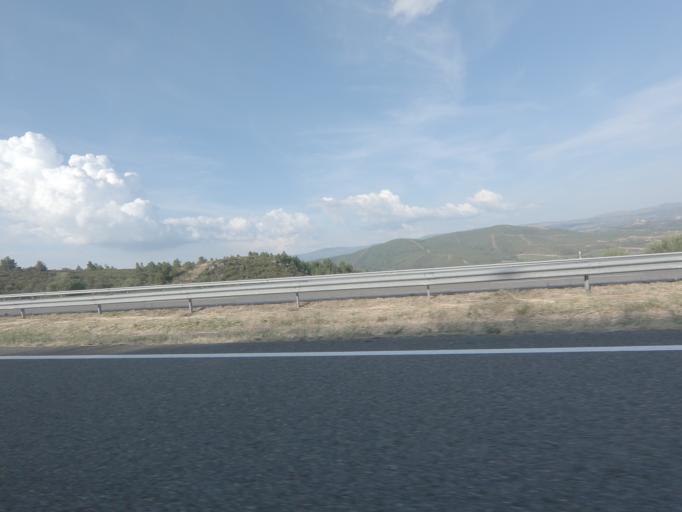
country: ES
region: Galicia
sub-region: Provincia de Ourense
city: Verin
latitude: 41.9535
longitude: -7.5100
